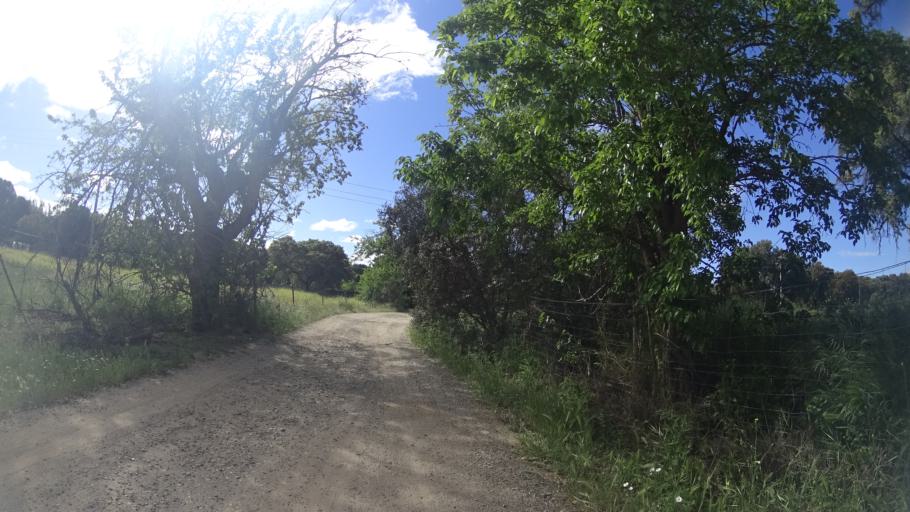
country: ES
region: Madrid
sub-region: Provincia de Madrid
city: Brunete
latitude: 40.4225
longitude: -3.9498
